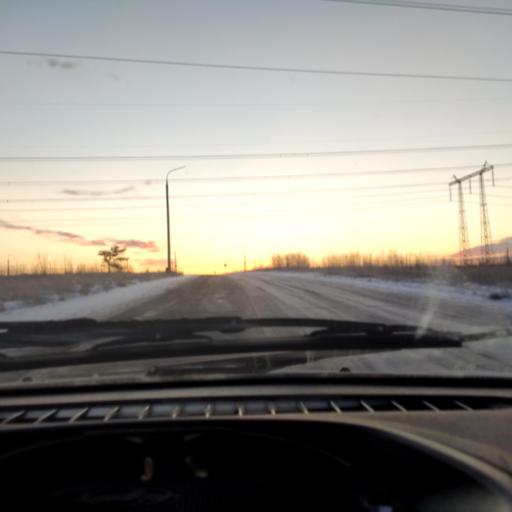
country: RU
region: Samara
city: Zhigulevsk
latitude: 53.5147
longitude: 49.5278
